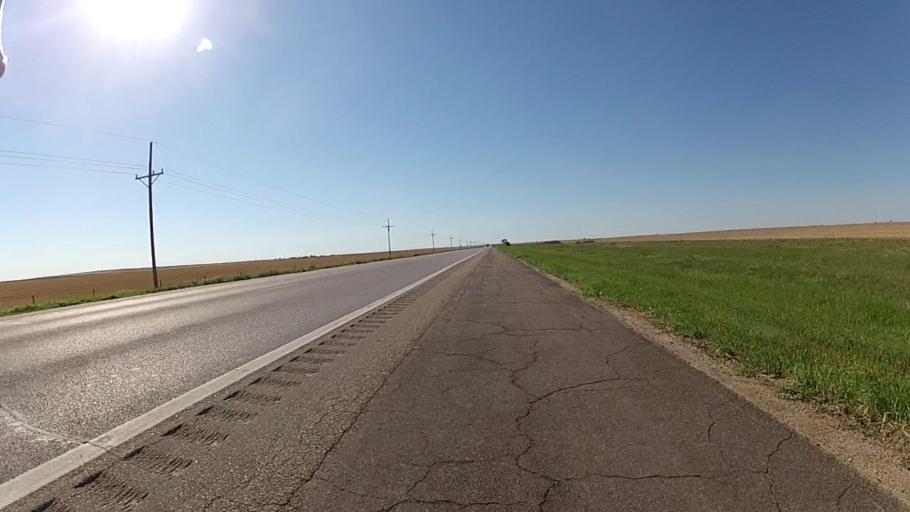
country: US
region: Kansas
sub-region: Ford County
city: Dodge City
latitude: 37.6004
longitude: -99.7011
